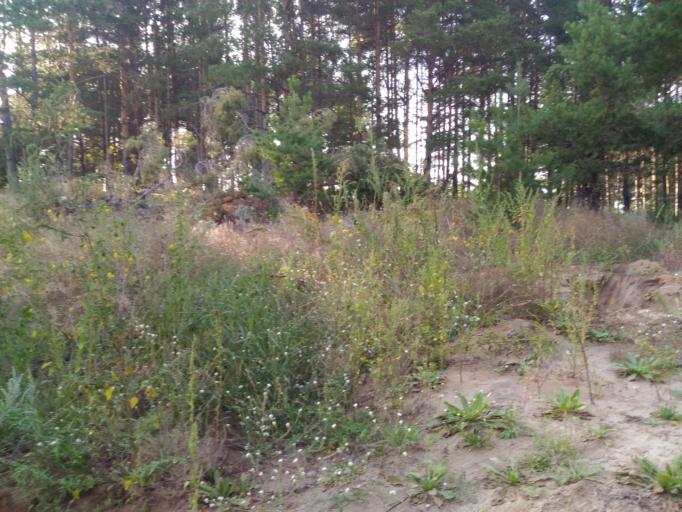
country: RU
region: Ulyanovsk
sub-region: Ulyanovskiy Rayon
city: Ulyanovsk
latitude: 54.3535
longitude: 48.5153
